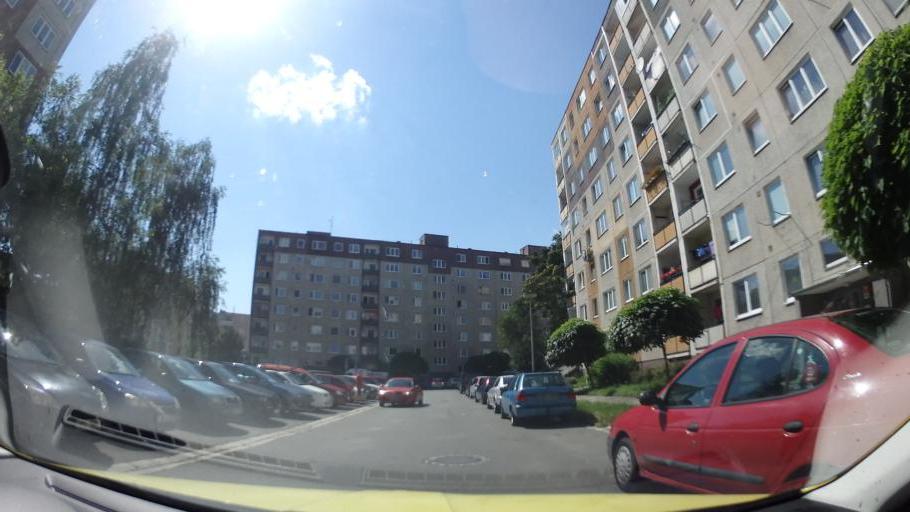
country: CZ
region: Olomoucky
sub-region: Okres Olomouc
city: Olomouc
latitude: 49.5728
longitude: 17.2543
